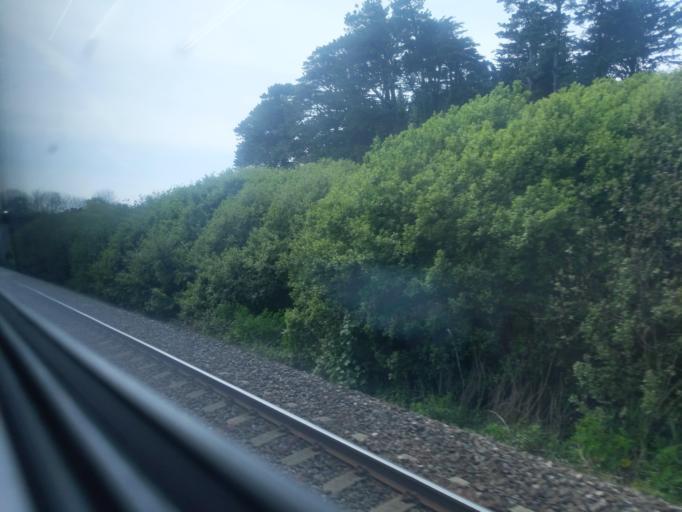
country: GB
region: England
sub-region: Cornwall
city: Marazion
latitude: 50.1361
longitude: -5.4752
